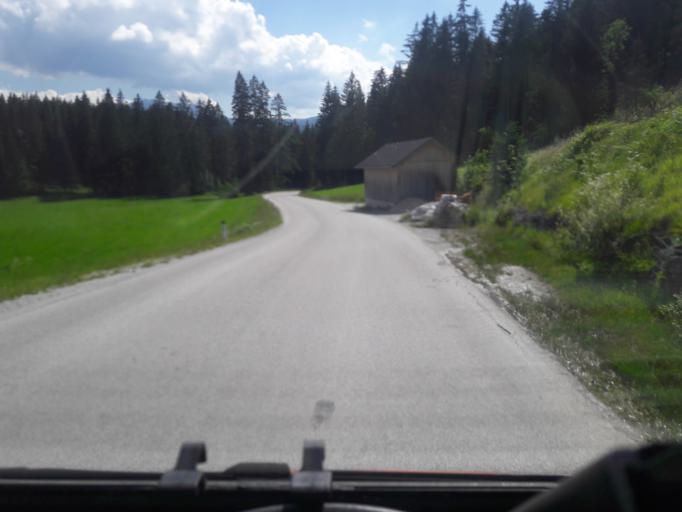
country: AT
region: Styria
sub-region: Politischer Bezirk Liezen
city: Tauplitz
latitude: 47.5603
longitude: 13.9472
